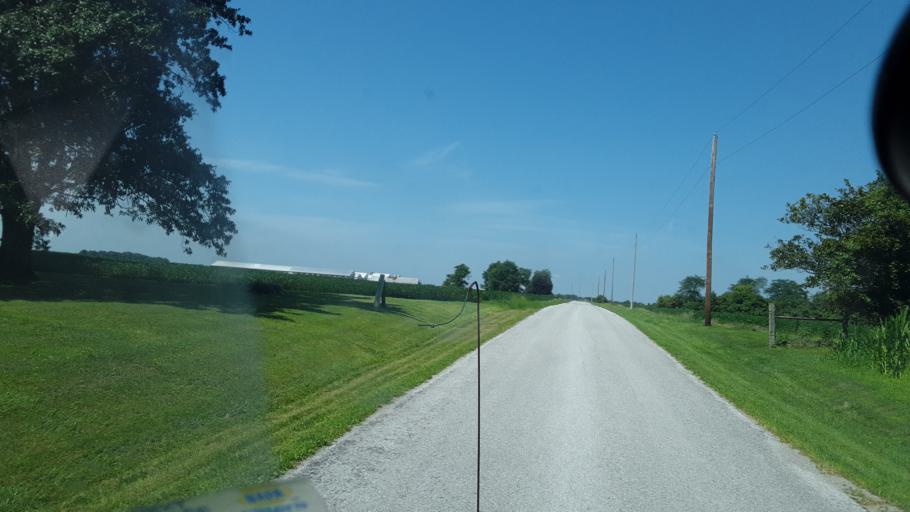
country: US
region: Ohio
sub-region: Wyandot County
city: Upper Sandusky
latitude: 40.9302
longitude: -83.2608
